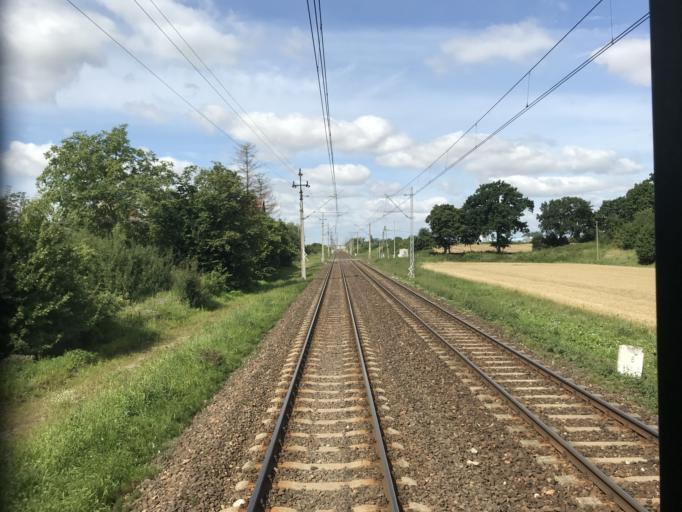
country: PL
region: Pomeranian Voivodeship
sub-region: Powiat malborski
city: Malbork
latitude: 54.0335
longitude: 19.0852
